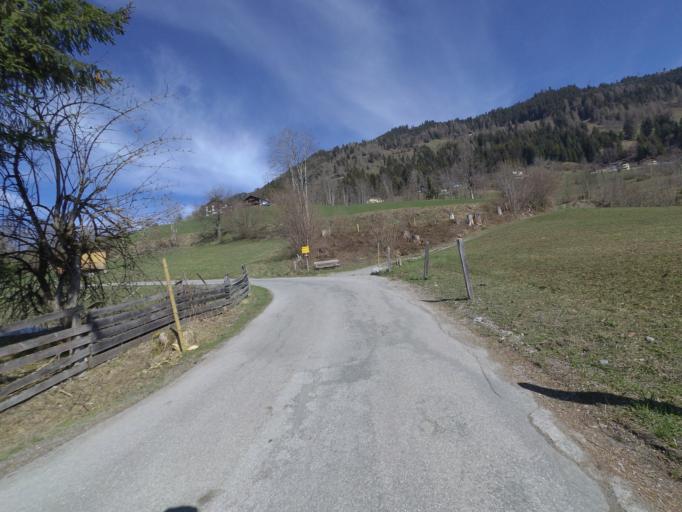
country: AT
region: Salzburg
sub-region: Politischer Bezirk Sankt Johann im Pongau
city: Sankt Veit im Pongau
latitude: 47.3355
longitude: 13.1374
